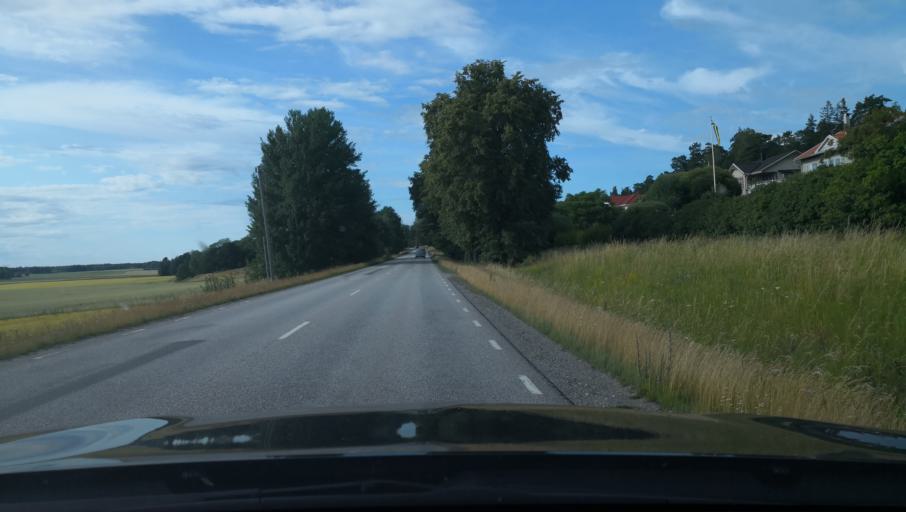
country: SE
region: Uppsala
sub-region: Habo Kommun
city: Balsta
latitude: 59.5962
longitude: 17.5102
